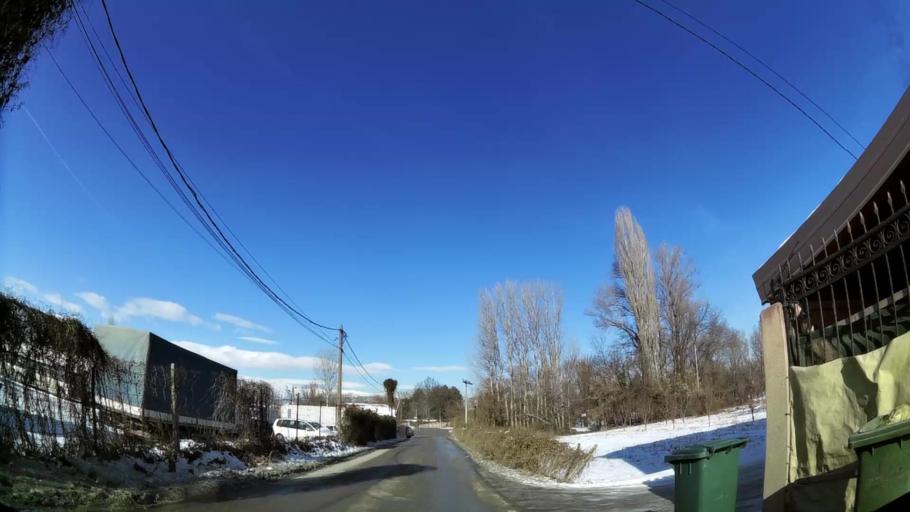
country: MK
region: Saraj
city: Saraj
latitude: 41.9979
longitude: 21.3428
